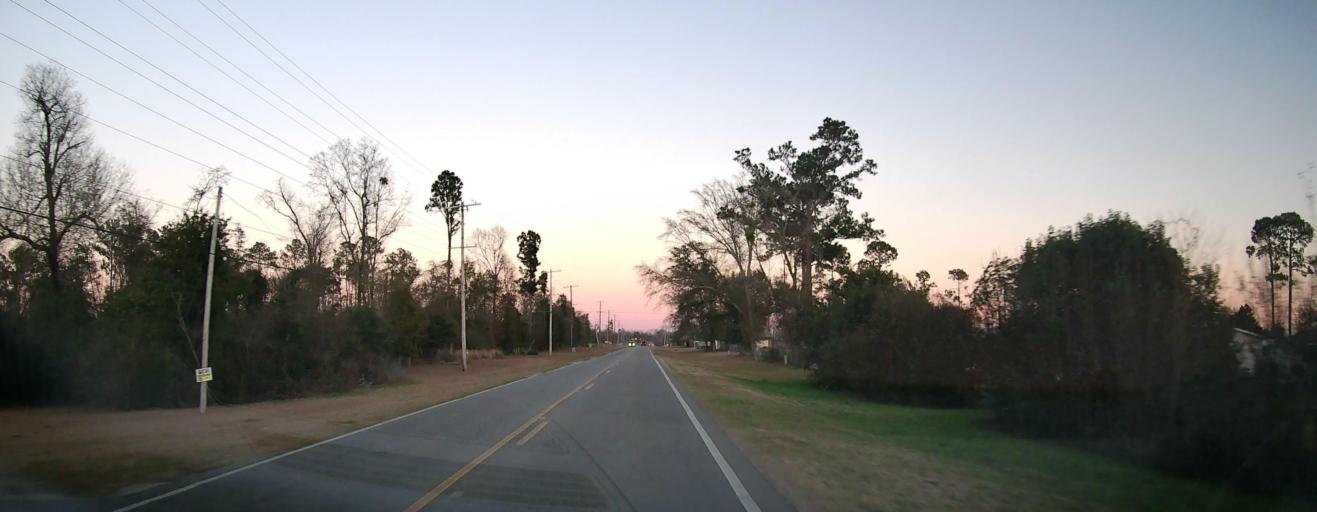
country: US
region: Georgia
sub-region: Dougherty County
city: Albany
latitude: 31.5292
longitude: -84.1229
